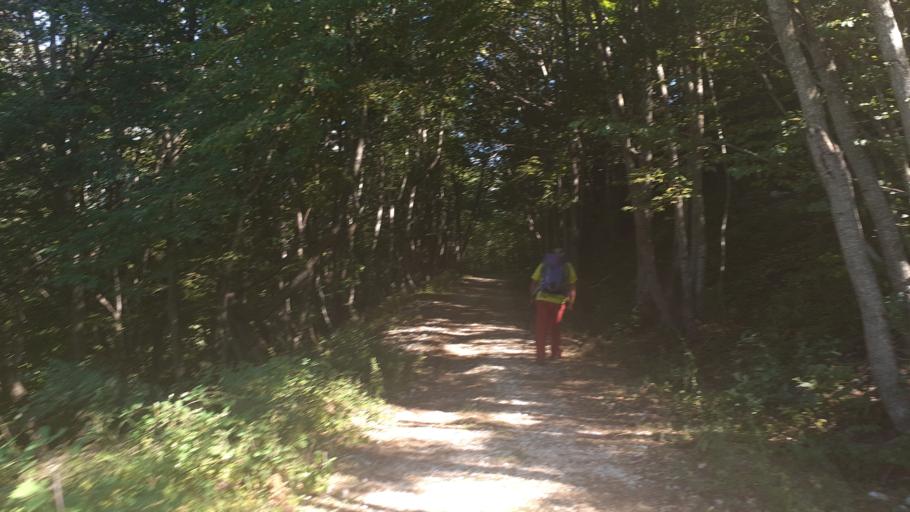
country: IT
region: Abruzzo
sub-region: Provincia di Pescara
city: Sant'Eufemia a Maiella
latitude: 42.1099
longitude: 13.9987
